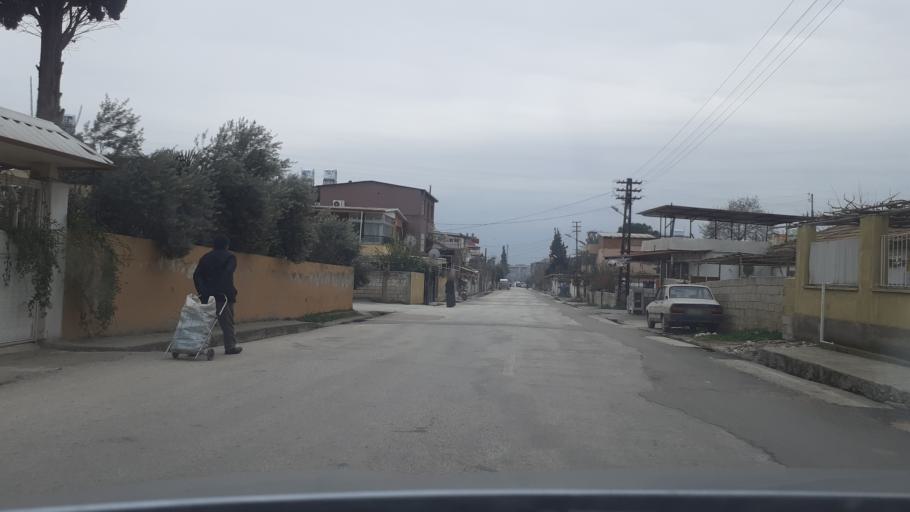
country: TR
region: Hatay
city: Kirikhan
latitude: 36.4904
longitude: 36.3558
